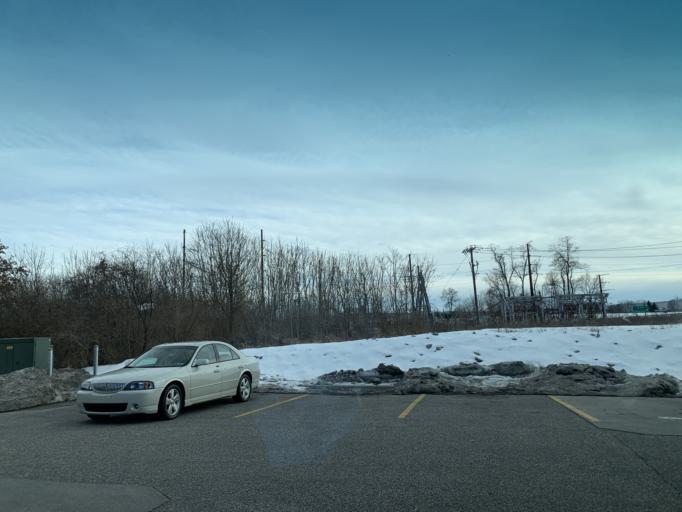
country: US
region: Pennsylvania
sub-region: Cumberland County
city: Carlisle
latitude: 40.1881
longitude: -77.2395
